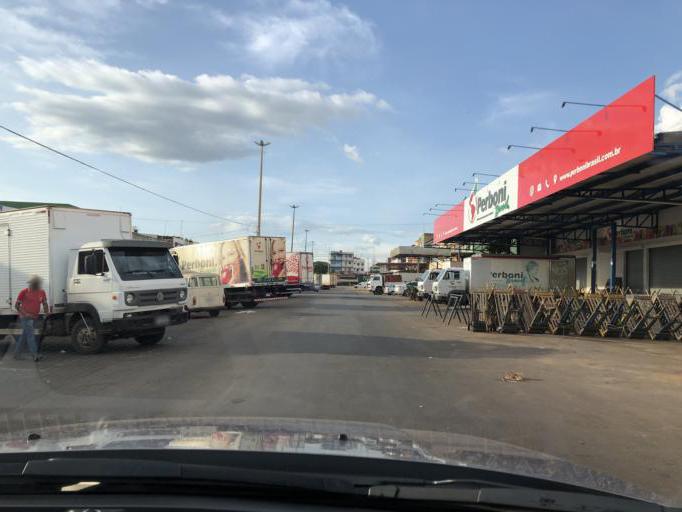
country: BR
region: Federal District
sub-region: Brasilia
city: Brasilia
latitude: -15.8247
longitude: -48.1227
